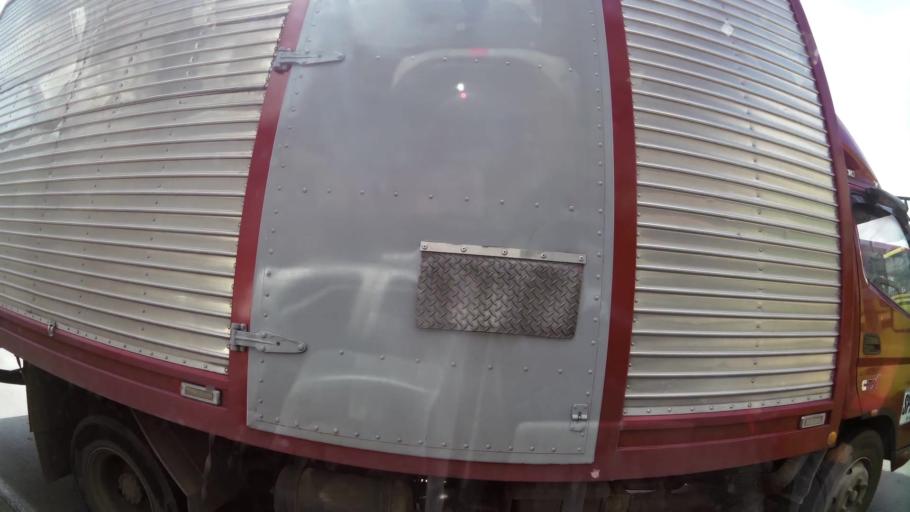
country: CO
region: Bogota D.C.
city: Bogota
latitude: 4.5702
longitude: -74.0996
